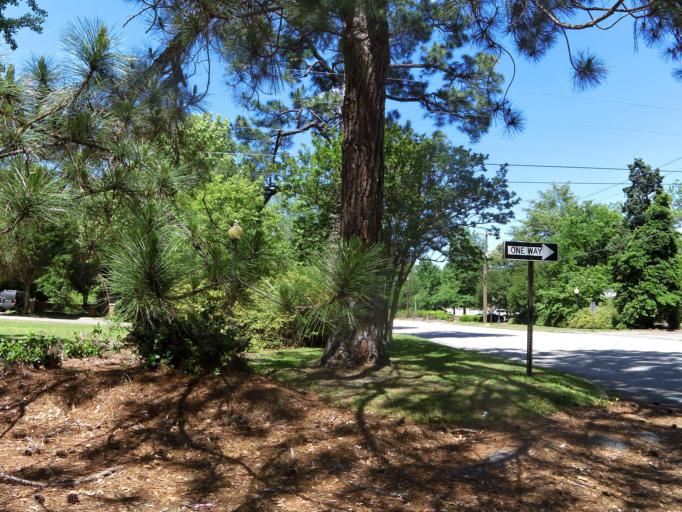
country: US
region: South Carolina
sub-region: Aiken County
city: Aiken
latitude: 33.5639
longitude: -81.7162
